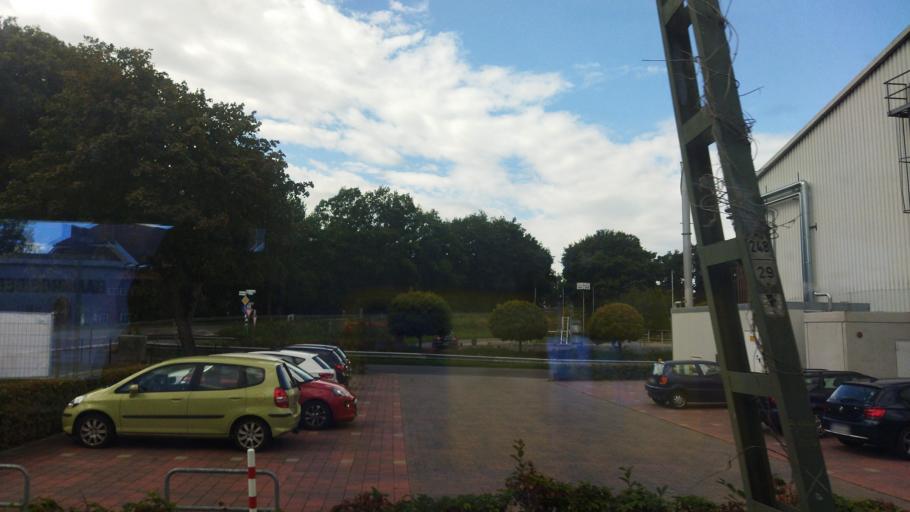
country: DE
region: Lower Saxony
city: Geeste
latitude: 52.5982
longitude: 7.3122
